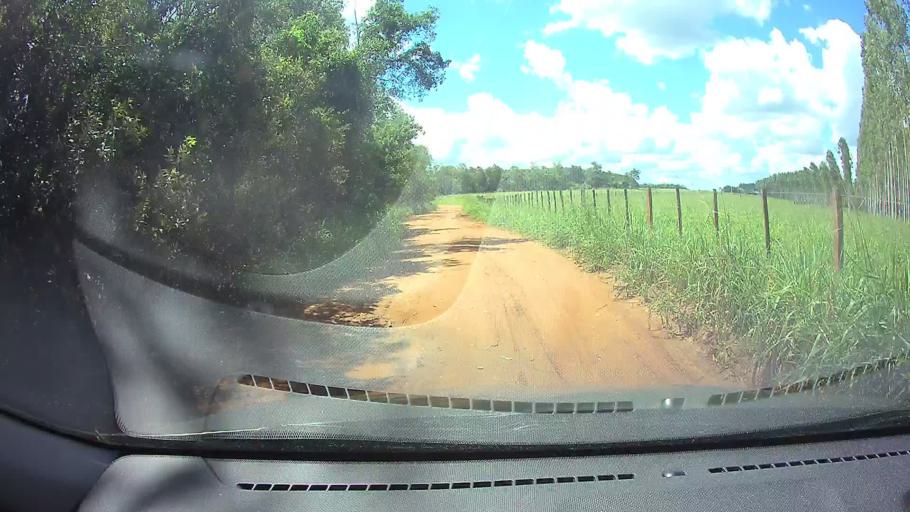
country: PY
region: Paraguari
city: La Colmena
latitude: -25.9634
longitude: -56.7372
